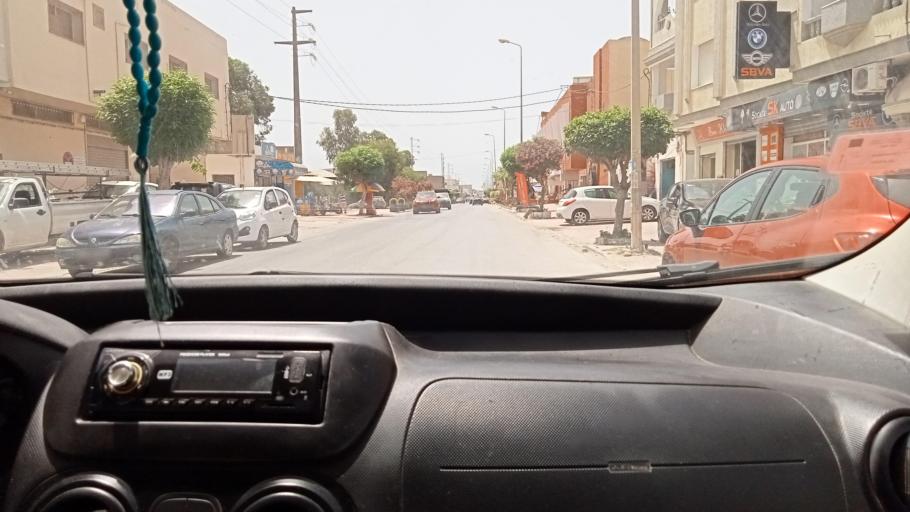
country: TN
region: Nabul
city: Qulaybiyah
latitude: 36.8588
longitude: 11.0905
